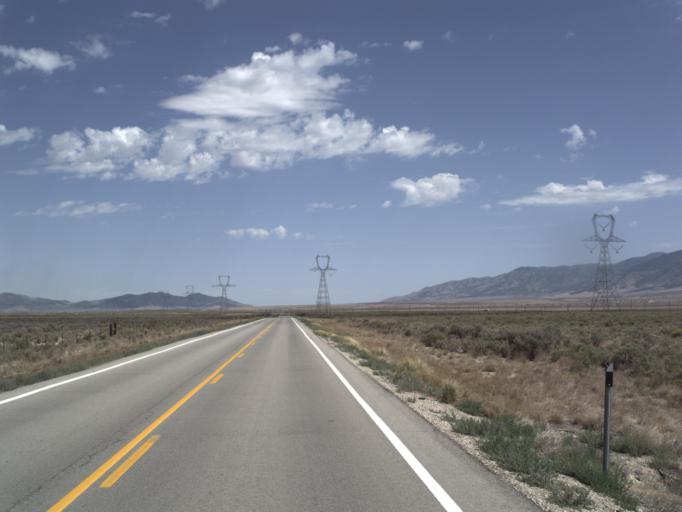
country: US
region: Utah
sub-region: Tooele County
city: Tooele
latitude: 40.2537
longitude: -112.3988
